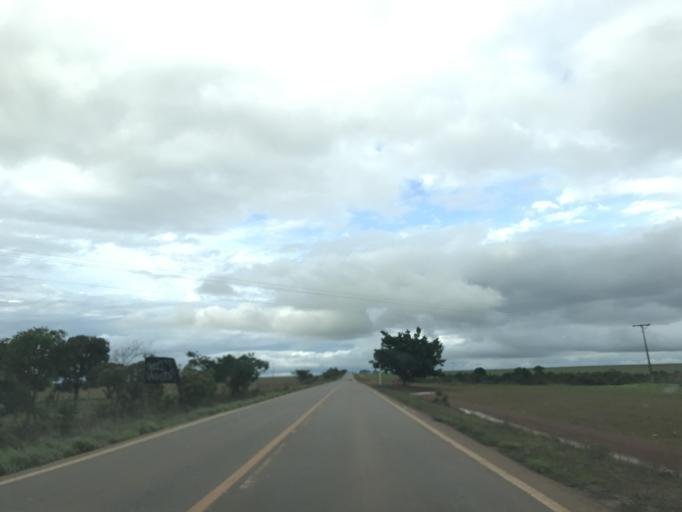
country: BR
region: Goias
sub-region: Luziania
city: Luziania
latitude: -16.4524
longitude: -48.2059
